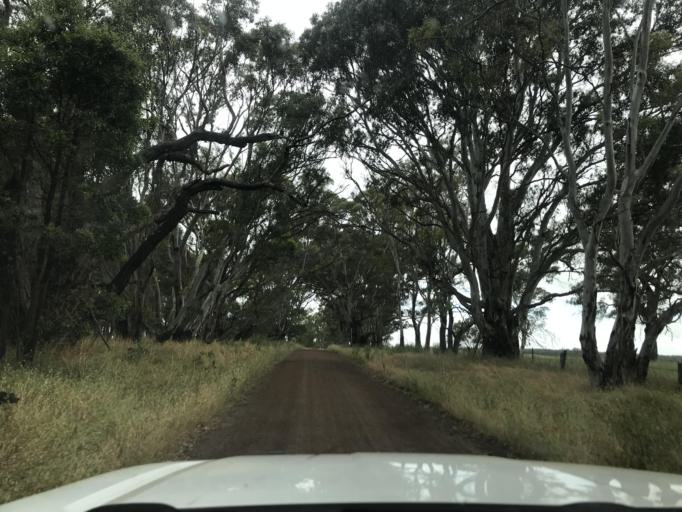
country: AU
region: South Australia
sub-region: Wattle Range
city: Penola
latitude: -37.2346
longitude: 141.4538
